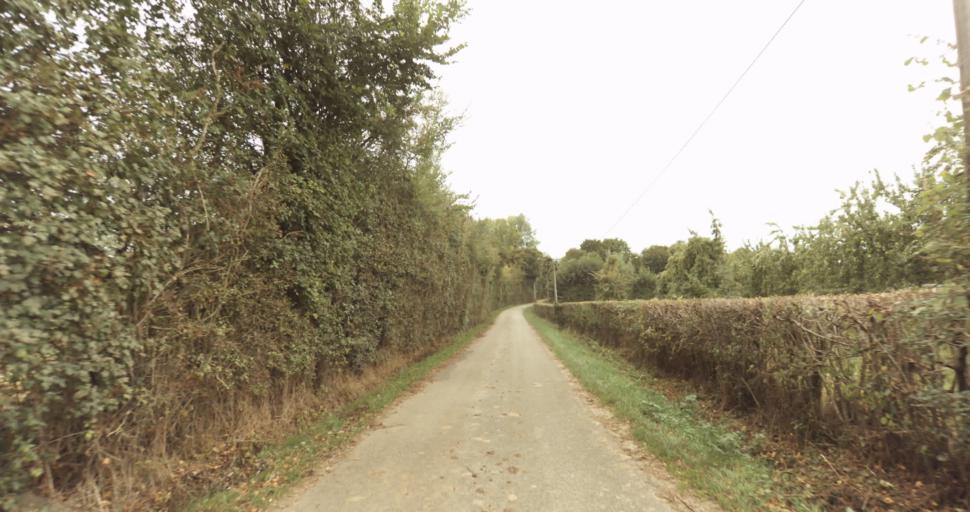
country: FR
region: Lower Normandy
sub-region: Departement de l'Orne
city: Gace
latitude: 48.7463
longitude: 0.3357
